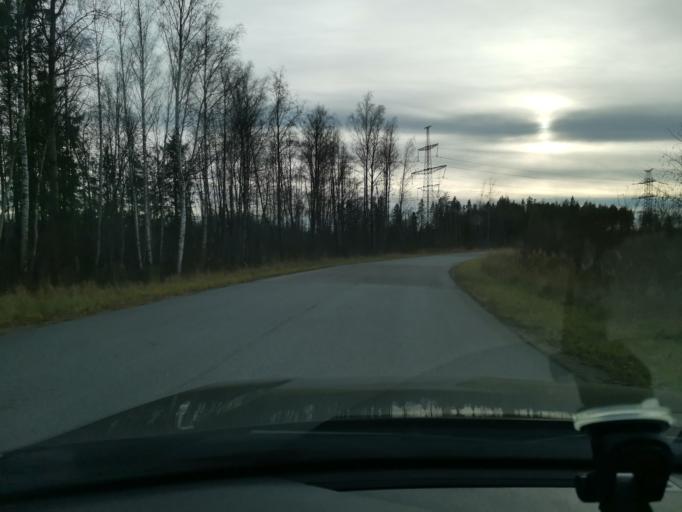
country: EE
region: Ida-Virumaa
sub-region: Sillamaee linn
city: Sillamae
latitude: 59.2702
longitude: 27.9139
